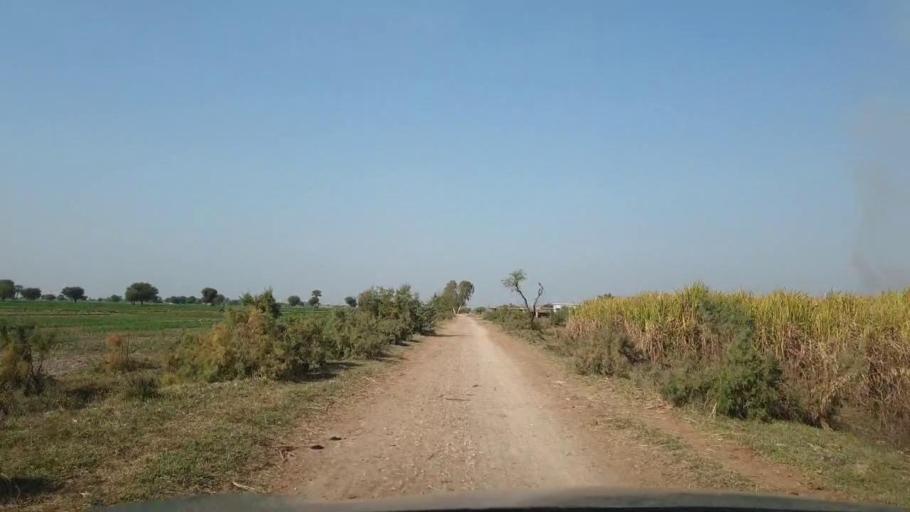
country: PK
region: Sindh
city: Berani
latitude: 25.6431
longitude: 68.8264
